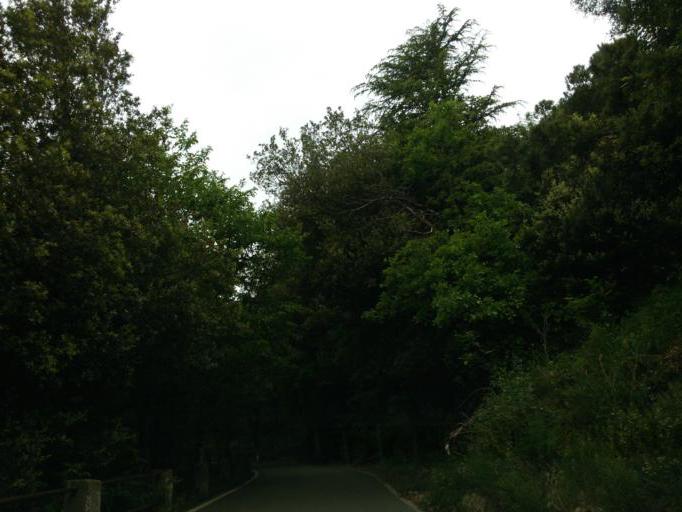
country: IT
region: Liguria
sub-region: Provincia di Genova
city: Genoa
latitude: 44.4376
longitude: 8.9312
